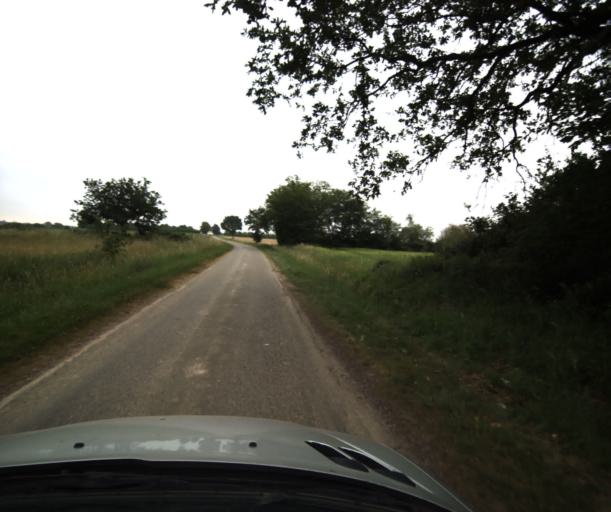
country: FR
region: Midi-Pyrenees
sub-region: Departement du Tarn-et-Garonne
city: Saint-Nicolas-de-la-Grave
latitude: 44.0542
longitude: 0.9975
